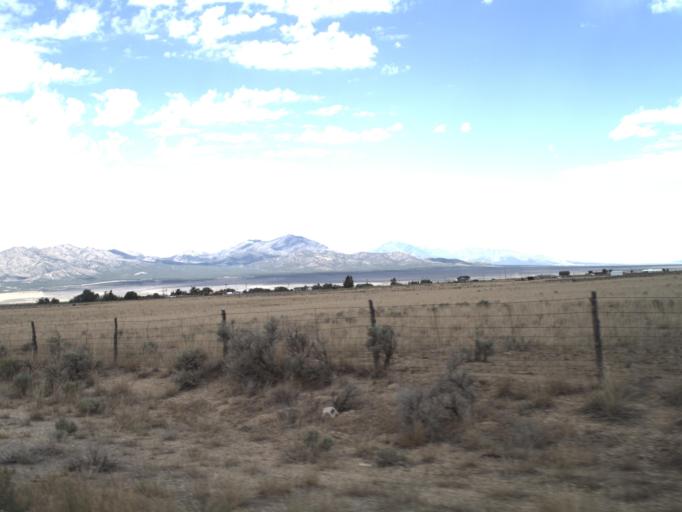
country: US
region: Utah
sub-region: Tooele County
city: Tooele
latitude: 40.0854
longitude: -112.4227
